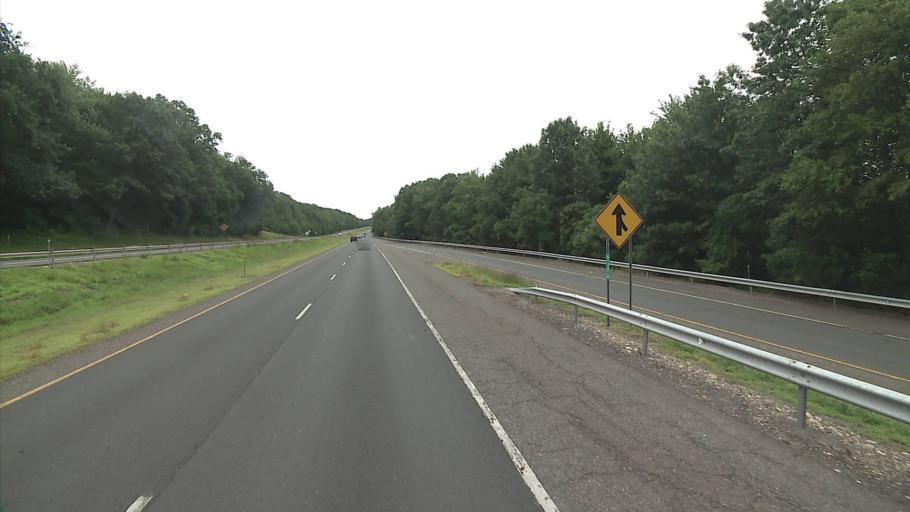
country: US
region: Connecticut
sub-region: New Haven County
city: Waterbury
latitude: 41.5860
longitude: -73.0555
